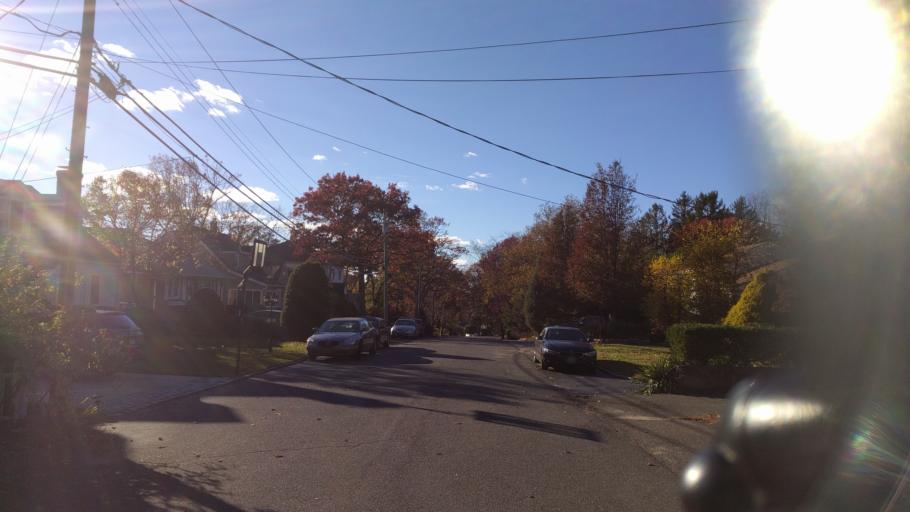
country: US
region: New York
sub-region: Nassau County
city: Bayville
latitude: 40.9066
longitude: -73.5687
